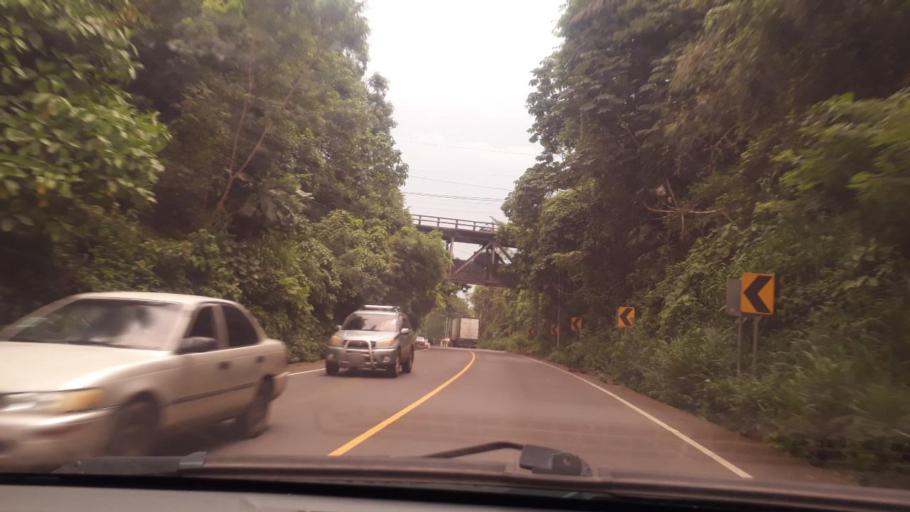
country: GT
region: Santa Rosa
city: Guazacapan
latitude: 14.0705
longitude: -90.4178
